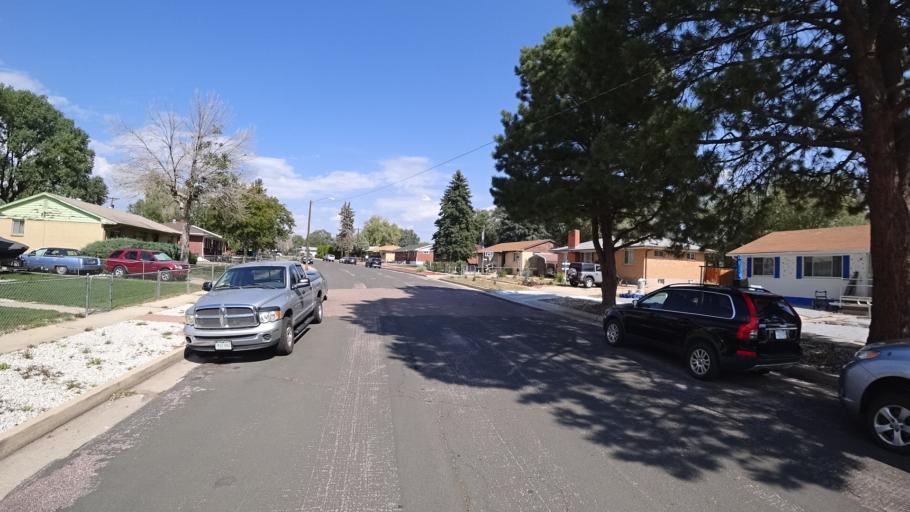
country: US
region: Colorado
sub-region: El Paso County
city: Colorado Springs
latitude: 38.8222
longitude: -104.7848
